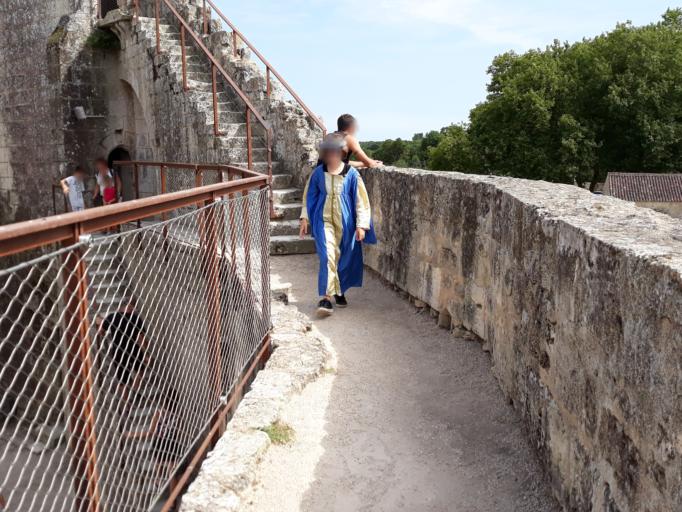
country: FR
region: Poitou-Charentes
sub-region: Departement de la Charente-Maritime
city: Saint-Agnant
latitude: 45.8207
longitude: -0.9510
